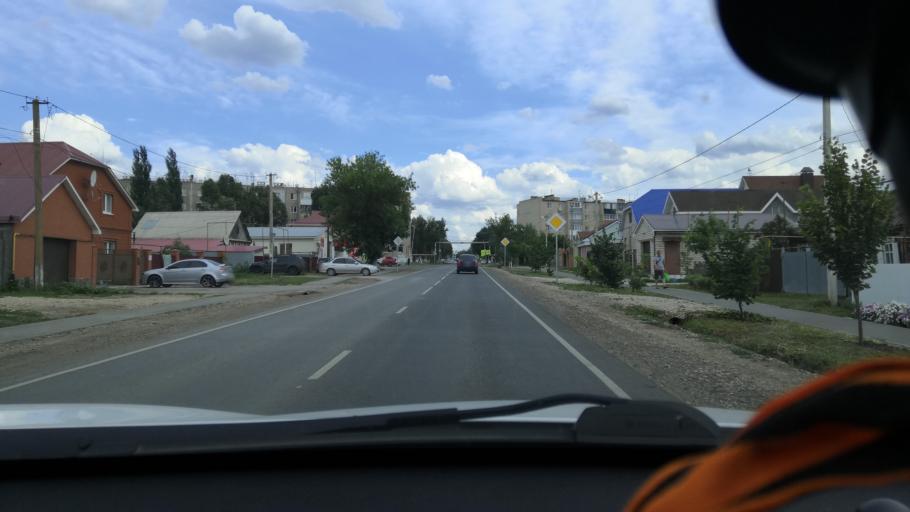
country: RU
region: Samara
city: Novosemeykino
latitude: 53.3728
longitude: 50.3501
